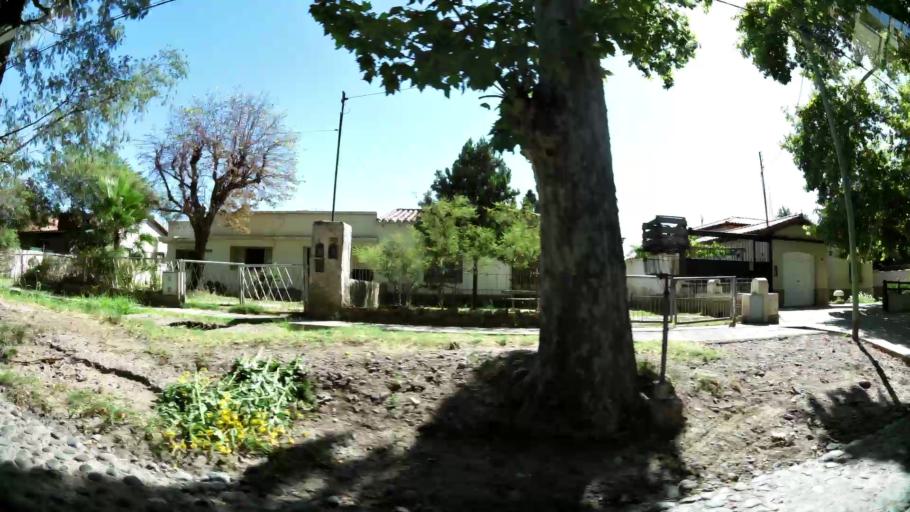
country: AR
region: Mendoza
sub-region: Departamento de Godoy Cruz
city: Godoy Cruz
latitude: -32.9466
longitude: -68.8032
